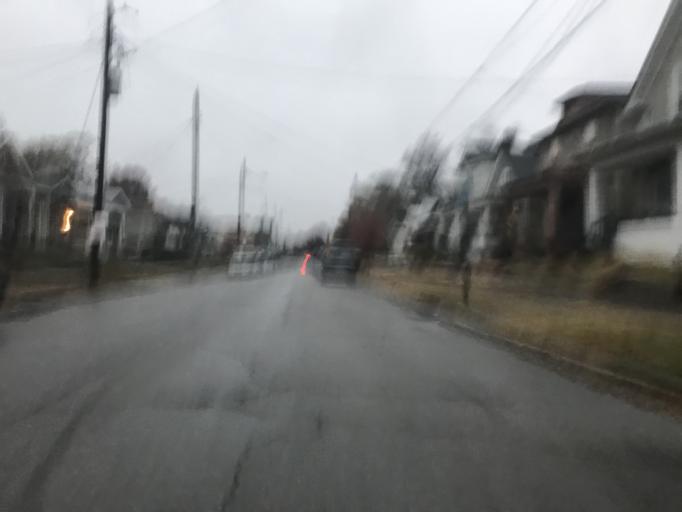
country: US
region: Kentucky
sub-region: Jefferson County
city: Louisville
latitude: 38.2314
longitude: -85.7447
